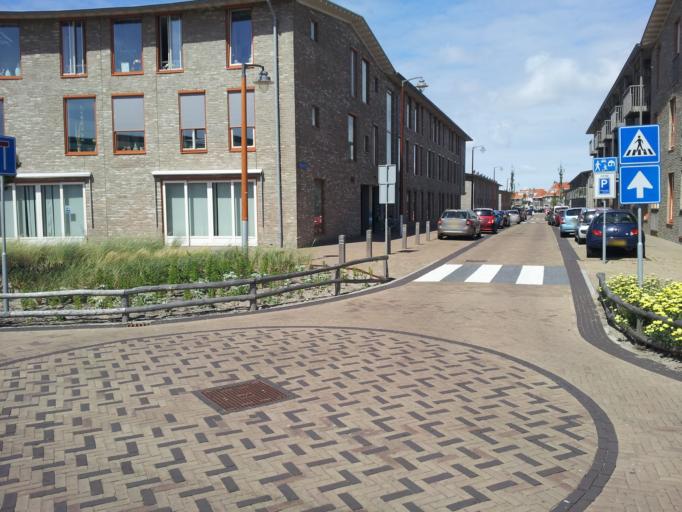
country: NL
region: South Holland
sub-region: Gemeente Katwijk
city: Katwijk aan Zee
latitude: 52.1980
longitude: 4.3908
